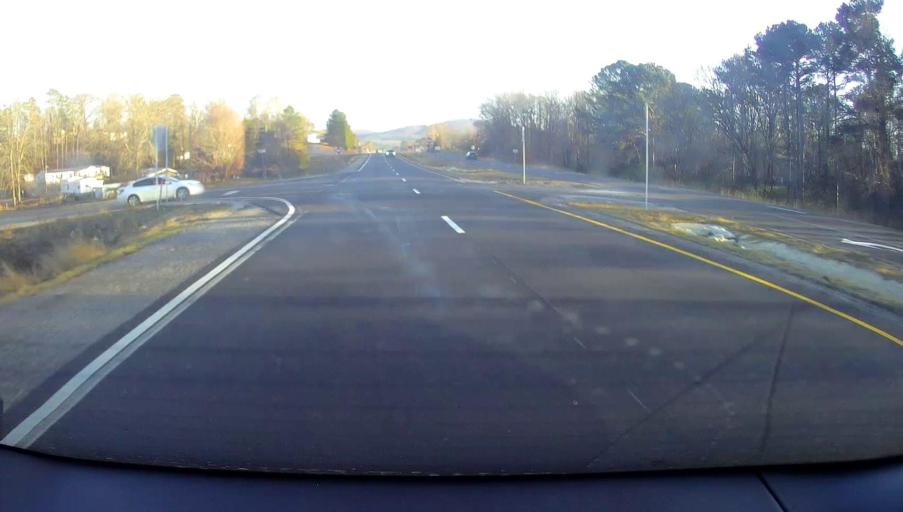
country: US
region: Alabama
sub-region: Calhoun County
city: Saks
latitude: 33.7099
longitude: -85.8389
